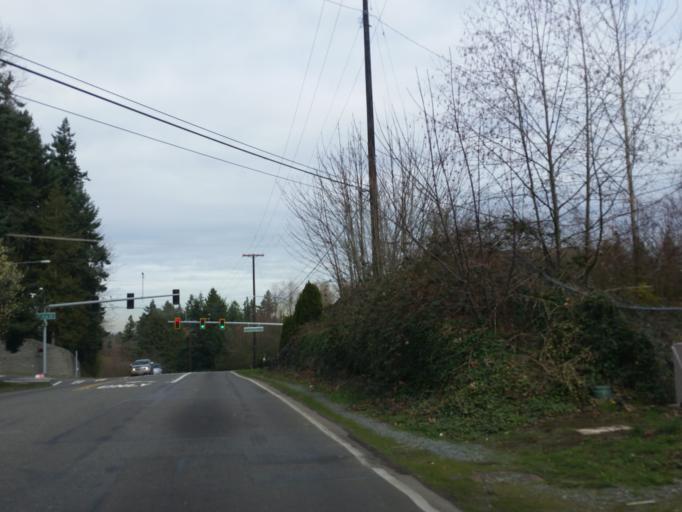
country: US
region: Washington
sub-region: Pierce County
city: Alderton
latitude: 47.1691
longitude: -122.2530
